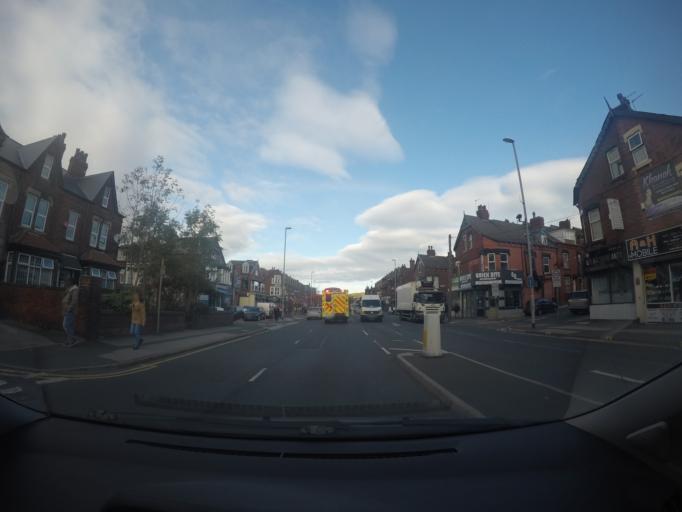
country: GB
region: England
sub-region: City and Borough of Leeds
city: Chapel Allerton
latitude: 53.8154
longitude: -1.5188
